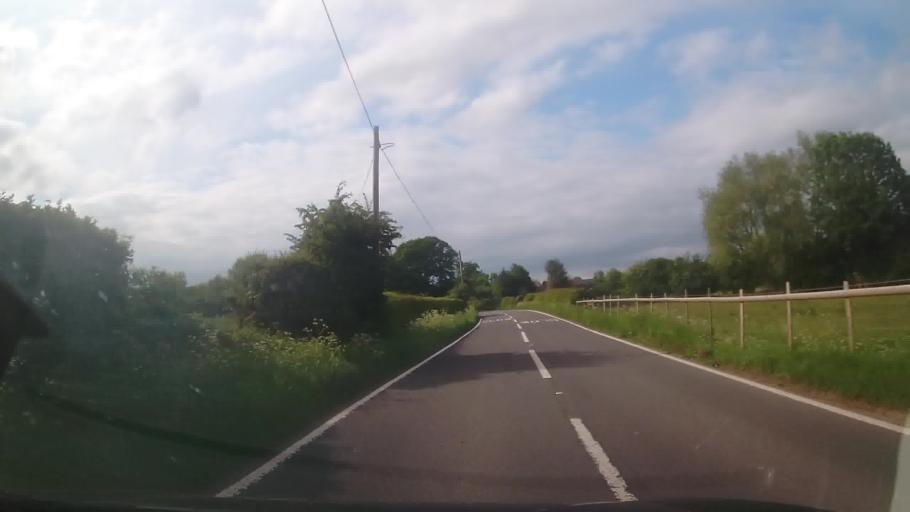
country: GB
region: England
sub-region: Shropshire
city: Petton
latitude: 52.8253
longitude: -2.8036
